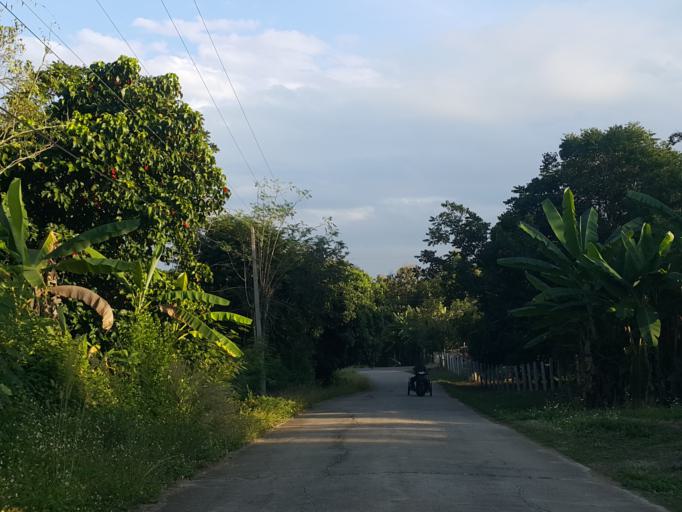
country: TH
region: Lampang
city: Lampang
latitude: 18.4182
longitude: 99.5506
